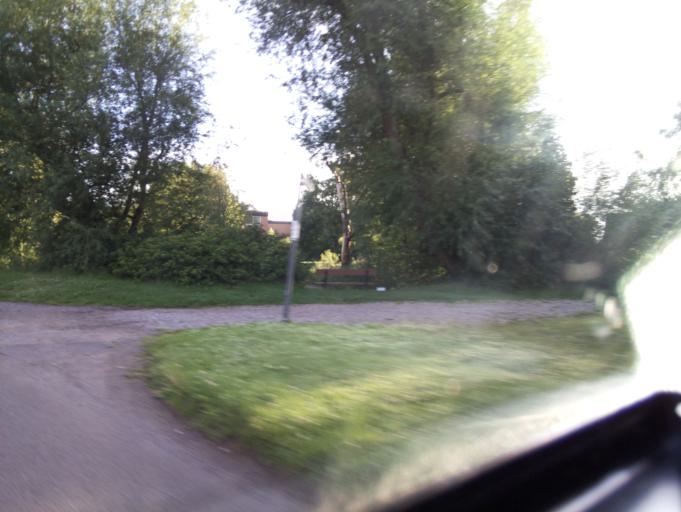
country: GB
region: England
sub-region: South Gloucestershire
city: Mangotsfield
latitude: 51.5017
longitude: -2.5178
